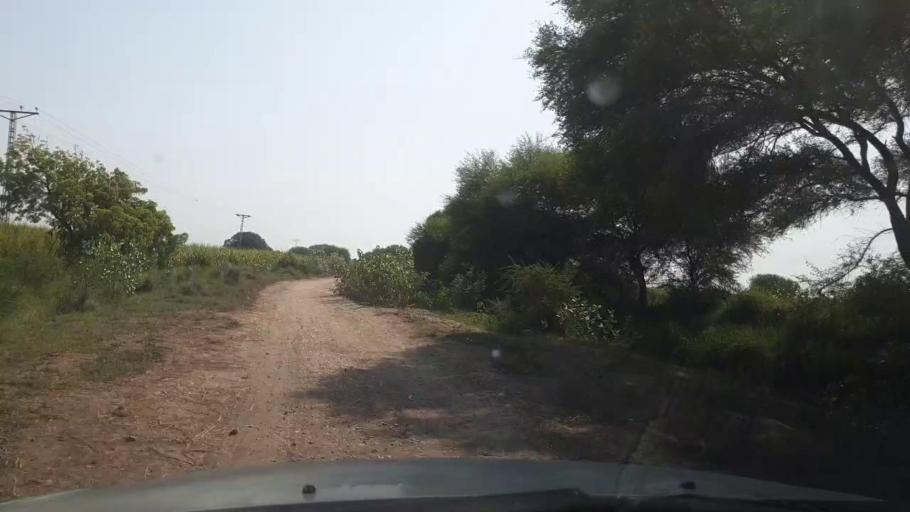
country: PK
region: Sindh
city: Bulri
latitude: 24.8671
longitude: 68.3108
